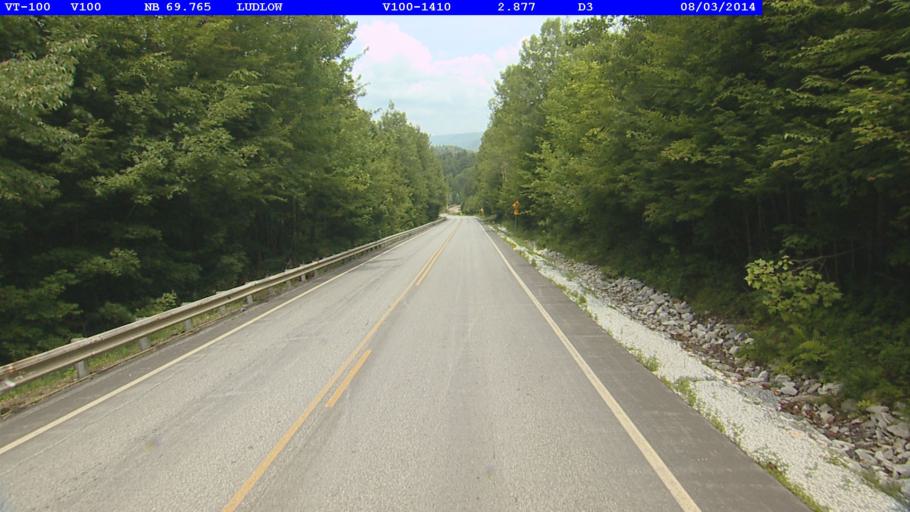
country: US
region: Vermont
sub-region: Windsor County
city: Chester
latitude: 43.3688
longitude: -72.7196
